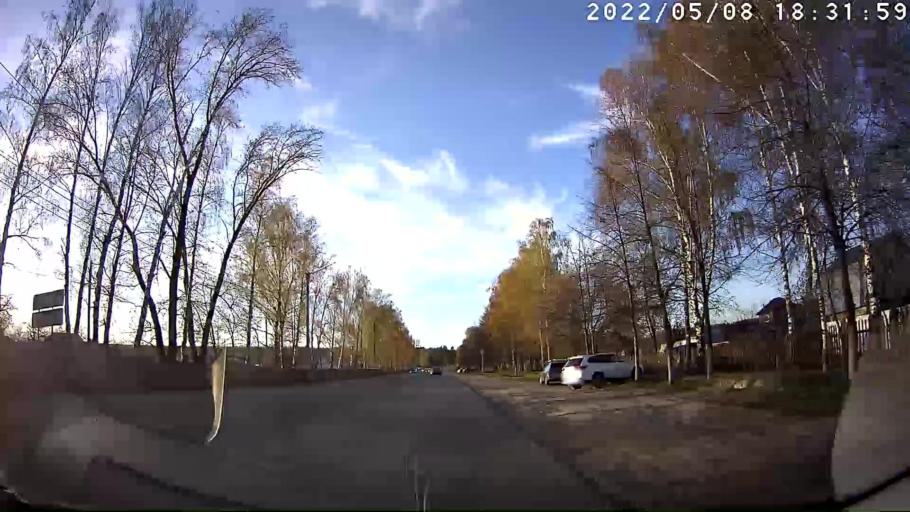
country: RU
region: Mariy-El
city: Volzhsk
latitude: 55.8844
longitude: 48.3600
